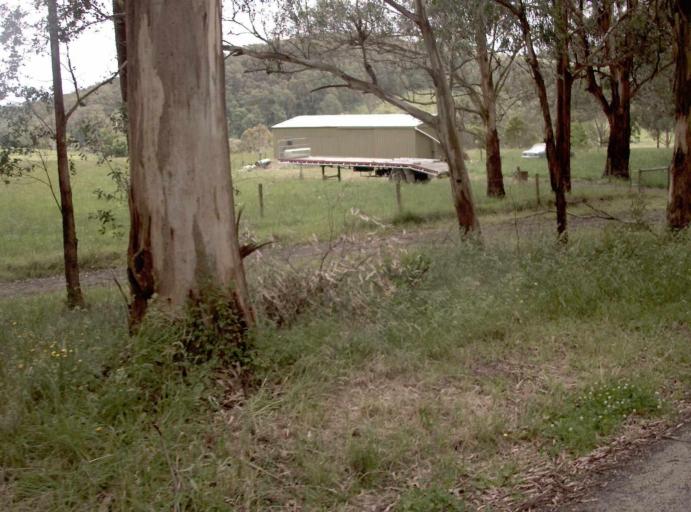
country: AU
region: Victoria
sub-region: Latrobe
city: Moe
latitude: -37.9927
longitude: 146.1460
